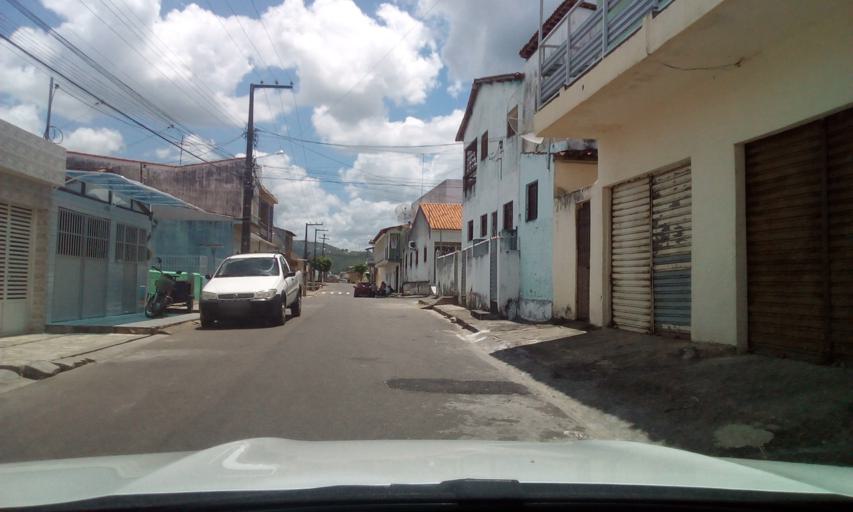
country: BR
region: Paraiba
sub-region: Guarabira
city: Guarabira
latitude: -6.8554
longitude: -35.4806
